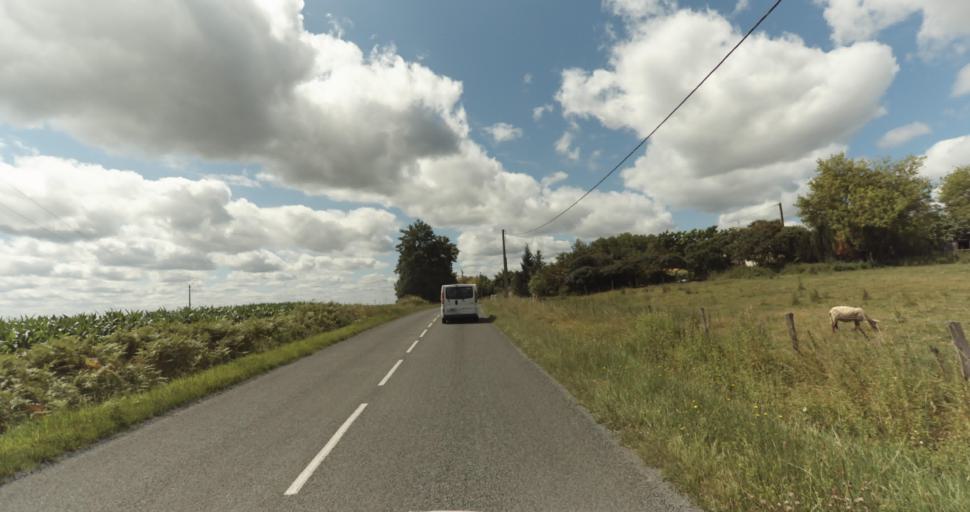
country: FR
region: Aquitaine
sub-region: Departement de la Gironde
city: Bazas
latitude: 44.4471
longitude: -0.2065
